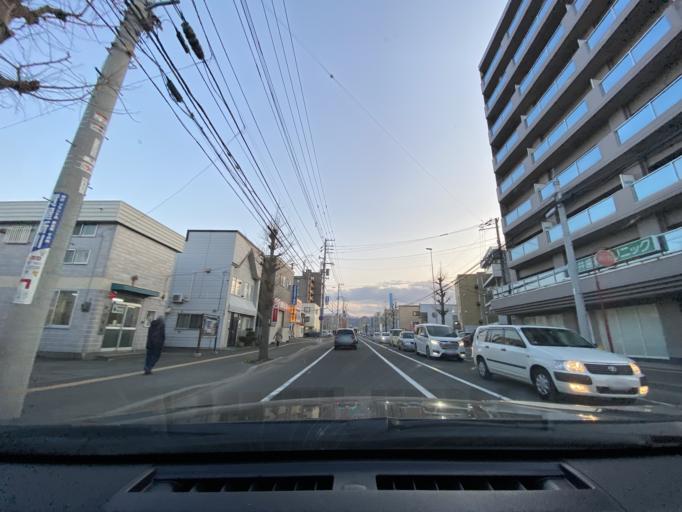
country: JP
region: Hokkaido
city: Sapporo
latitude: 43.0949
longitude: 141.3223
